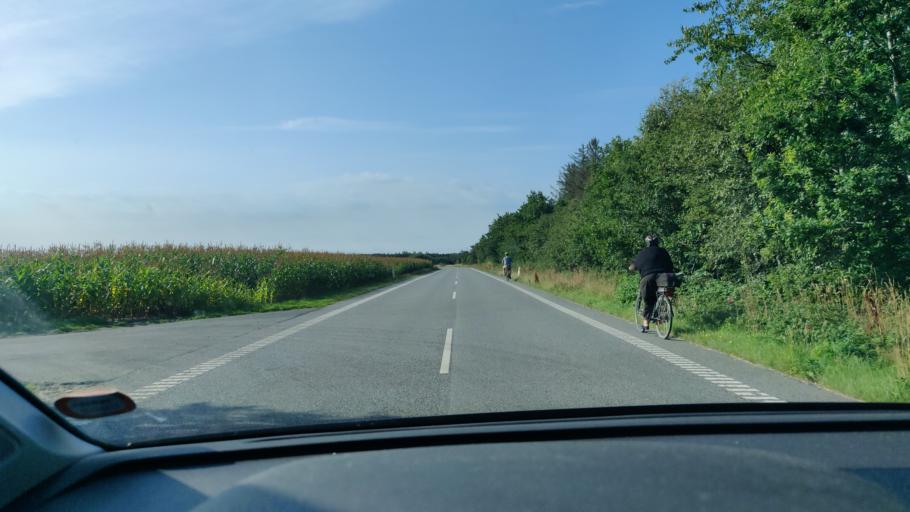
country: DK
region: North Denmark
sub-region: Jammerbugt Kommune
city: Pandrup
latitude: 57.2497
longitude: 9.6457
